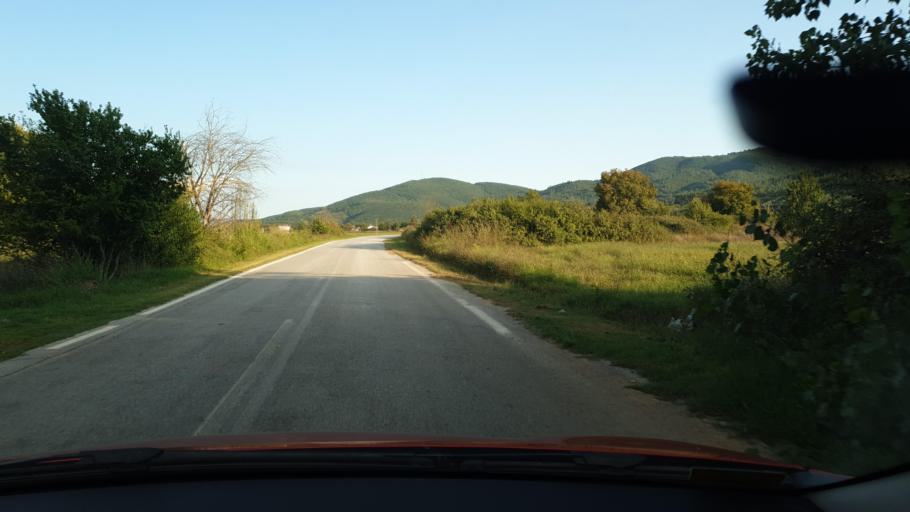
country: GR
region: Central Macedonia
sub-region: Nomos Chalkidikis
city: Galatista
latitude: 40.5640
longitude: 23.2925
